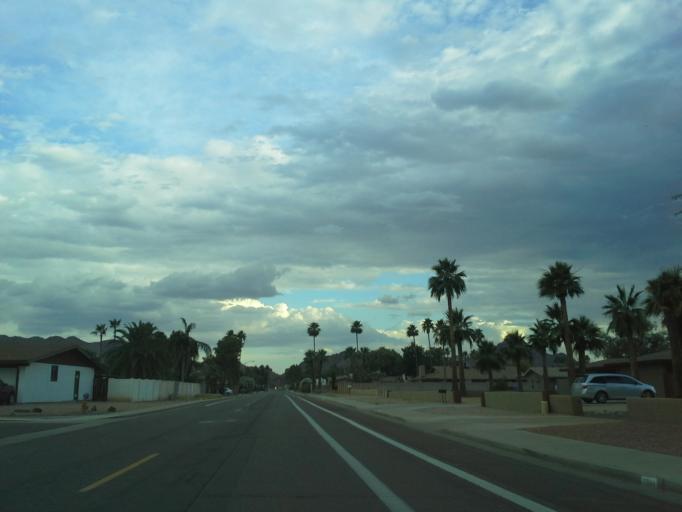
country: US
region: Arizona
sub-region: Maricopa County
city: Paradise Valley
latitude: 33.5878
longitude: -112.0045
